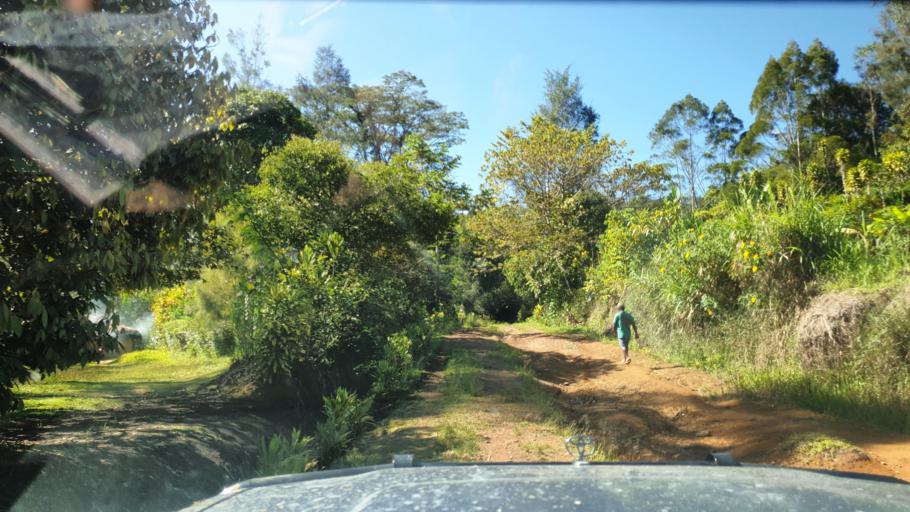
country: PG
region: Western Highlands
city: Rauna
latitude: -5.8024
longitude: 144.3686
